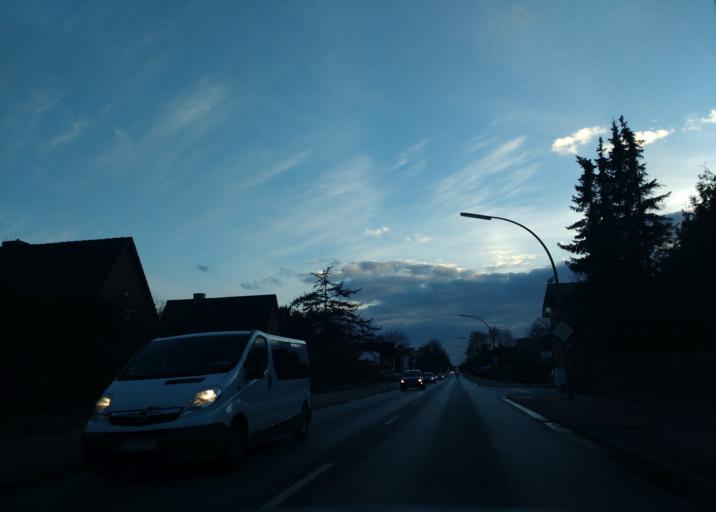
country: DE
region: Schleswig-Holstein
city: Norderstedt
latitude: 53.6797
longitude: 9.9935
